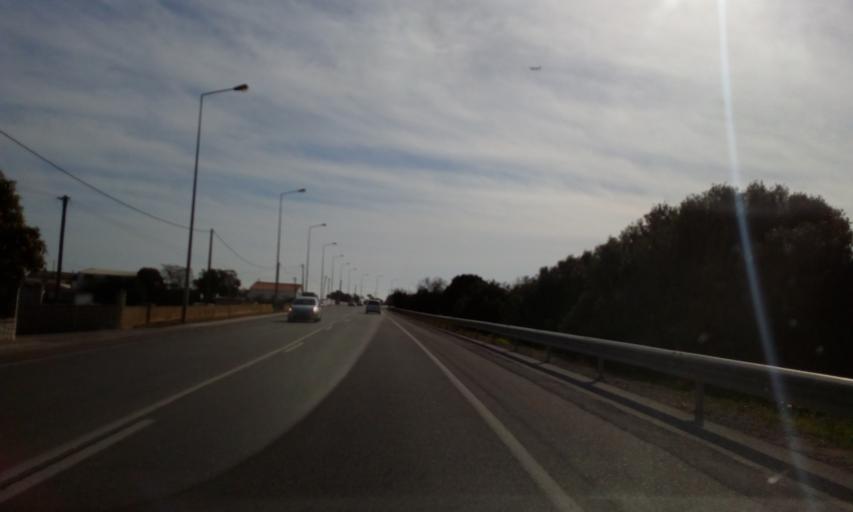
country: PT
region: Faro
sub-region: Faro
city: Faro
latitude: 37.0233
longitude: -7.9168
